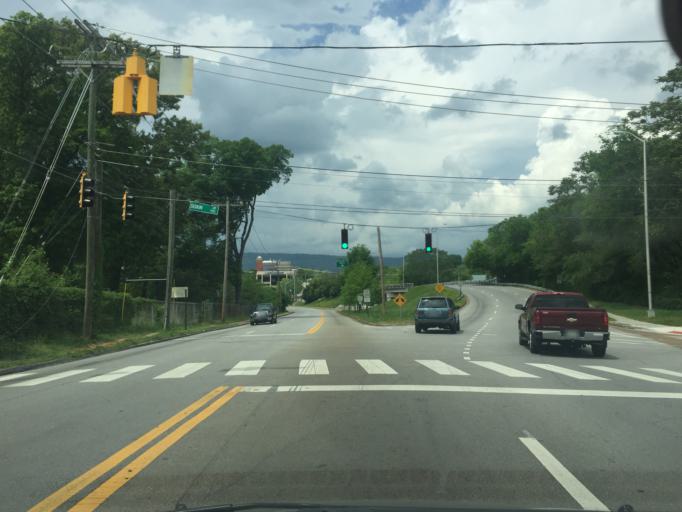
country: US
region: Tennessee
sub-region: Hamilton County
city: Chattanooga
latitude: 35.0501
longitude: -85.2959
